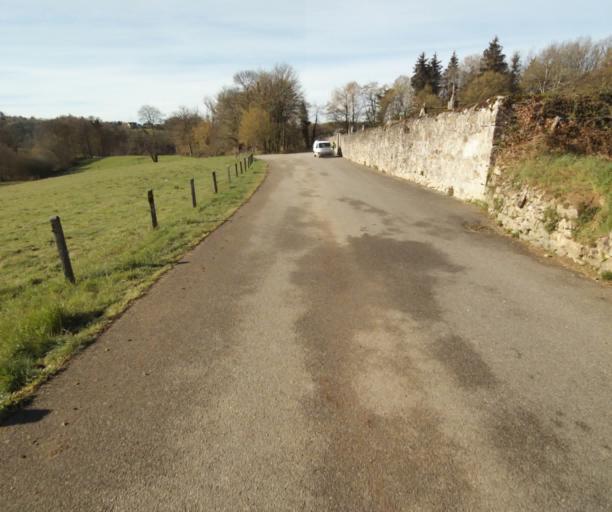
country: FR
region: Limousin
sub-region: Departement de la Correze
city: Laguenne
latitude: 45.2650
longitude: 1.8705
